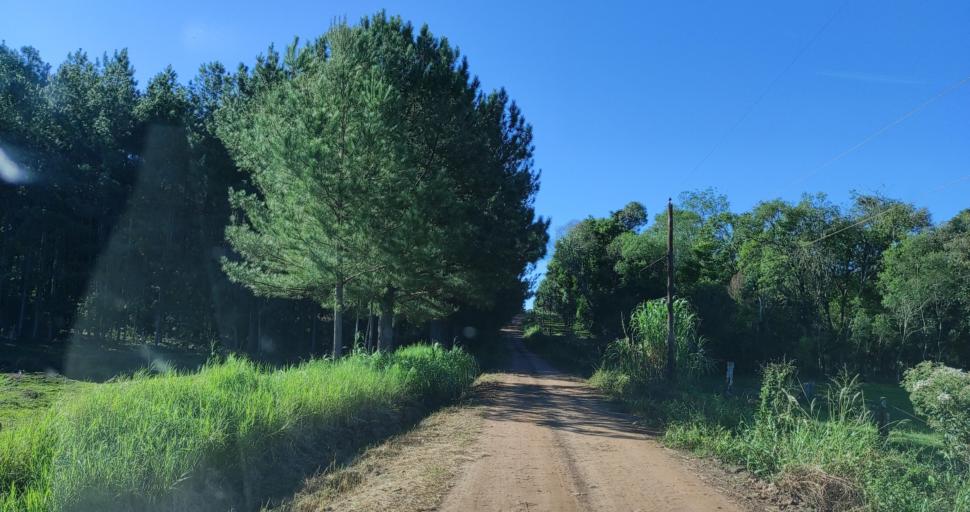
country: AR
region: Misiones
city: Capiovi
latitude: -26.9216
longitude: -55.0003
